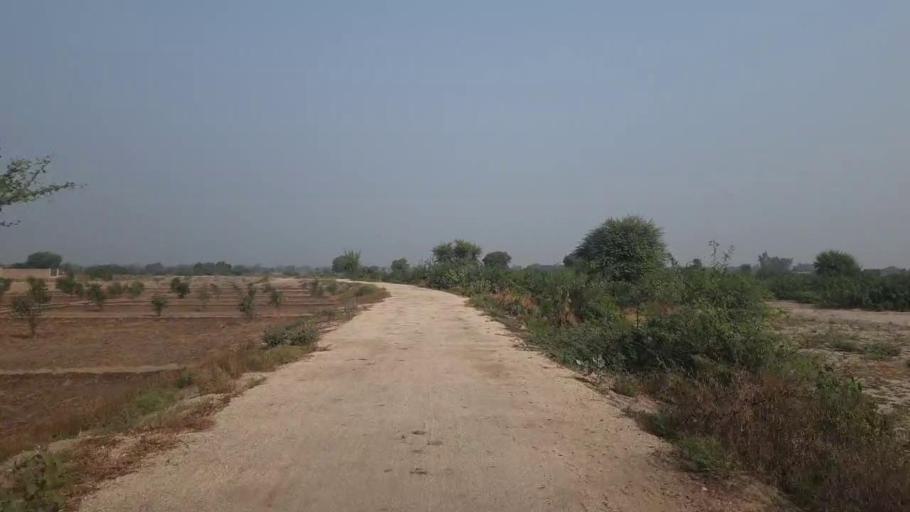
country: PK
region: Sindh
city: Tando Jam
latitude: 25.3281
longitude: 68.5240
